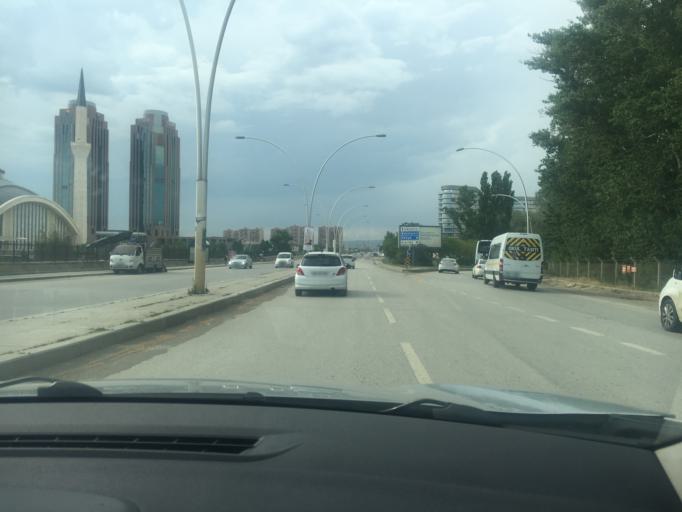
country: TR
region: Ankara
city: Batikent
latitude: 39.9054
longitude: 32.7649
